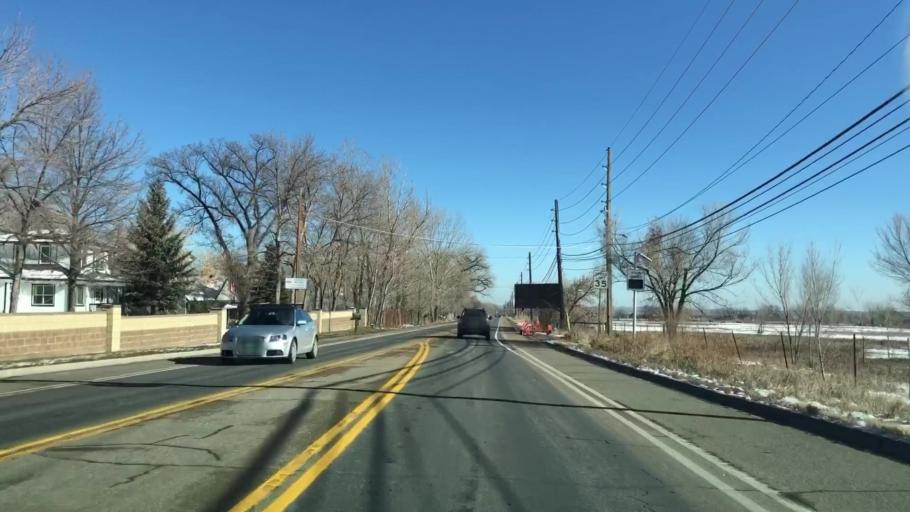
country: US
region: Colorado
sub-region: Boulder County
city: Boulder
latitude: 40.0510
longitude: -105.2427
